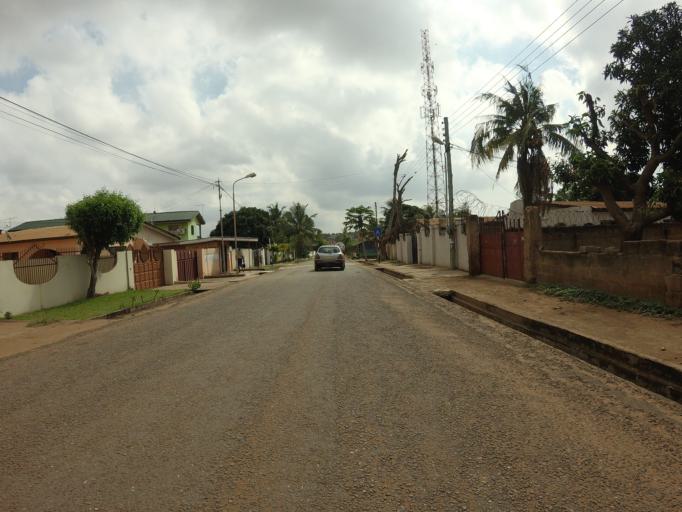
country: GH
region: Greater Accra
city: Nungua
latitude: 5.6126
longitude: -0.1026
